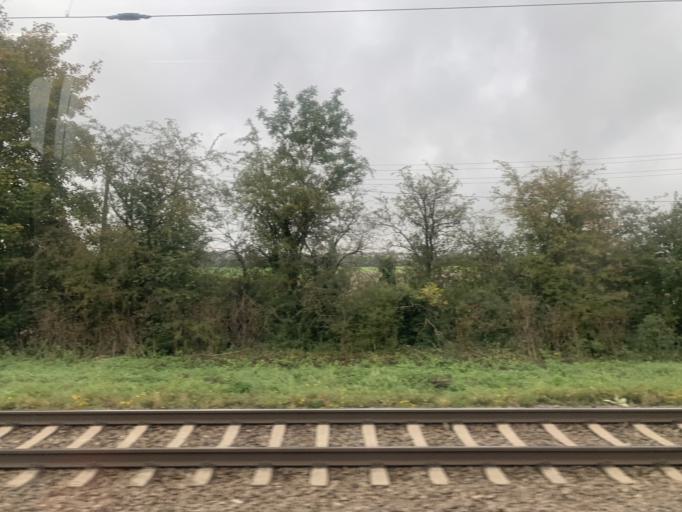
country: DE
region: Bavaria
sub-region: Upper Bavaria
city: Oberschleissheim
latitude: 48.2210
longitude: 11.5417
